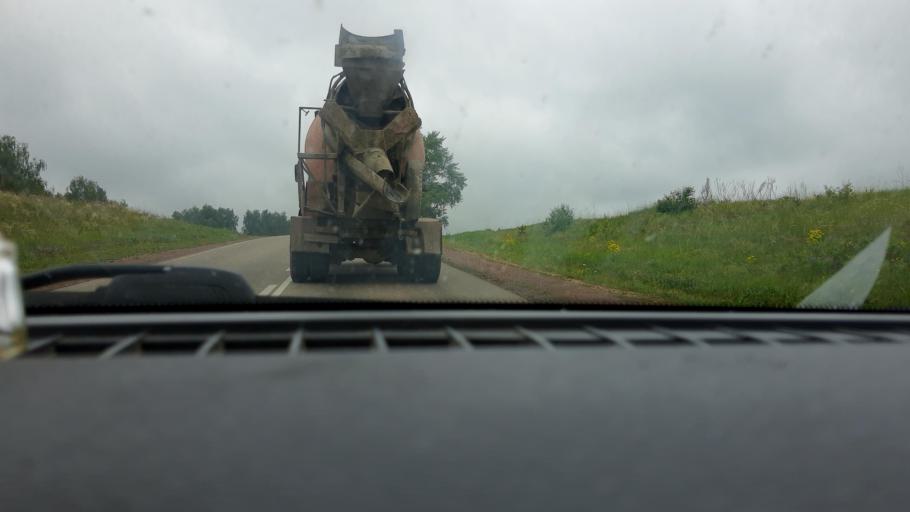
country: RU
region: Bashkortostan
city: Belebey
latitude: 54.0651
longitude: 54.0595
